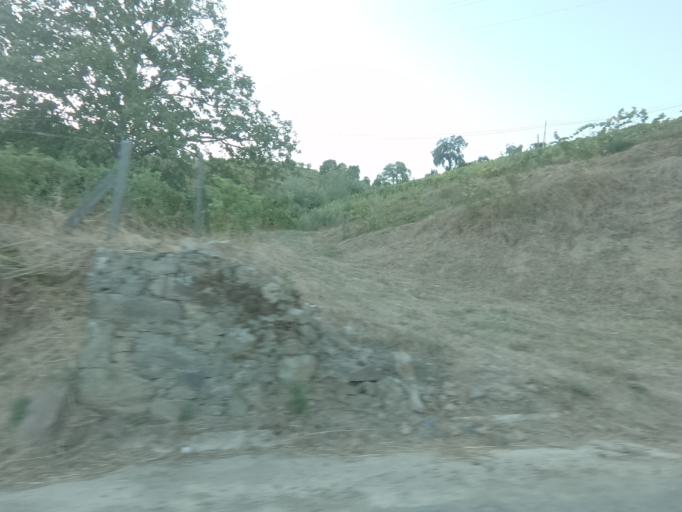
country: PT
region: Vila Real
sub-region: Mesao Frio
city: Mesao Frio
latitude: 41.1799
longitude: -7.8564
